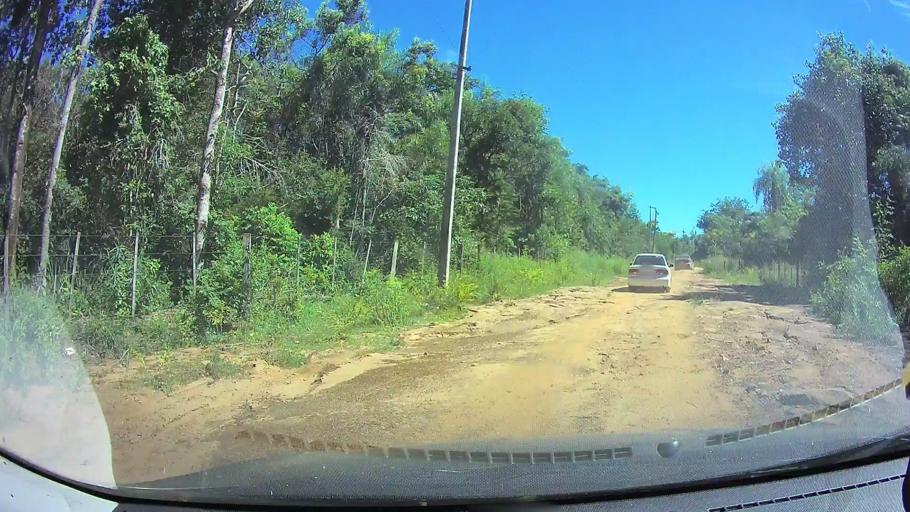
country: PY
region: Cordillera
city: Arroyos y Esteros
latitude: -24.9778
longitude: -57.2151
